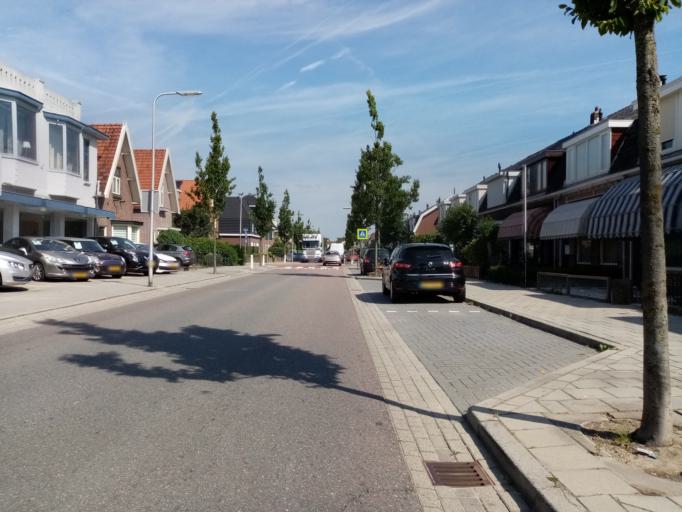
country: NL
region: South Holland
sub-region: Gemeente Katwijk
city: Rijnsburg
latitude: 52.1914
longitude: 4.4475
